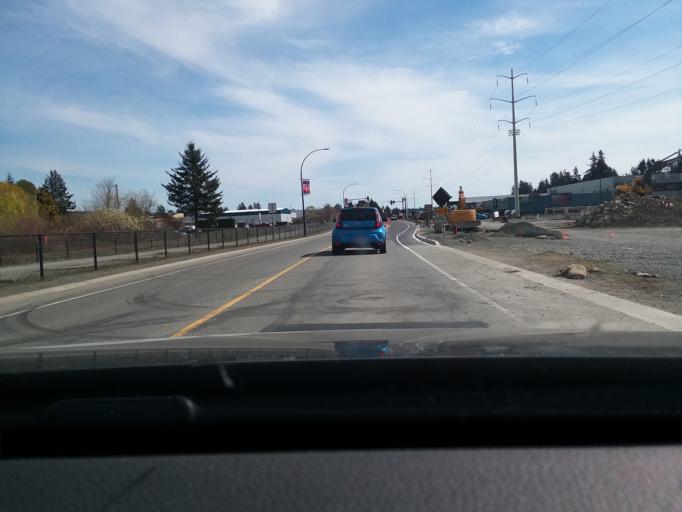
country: CA
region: British Columbia
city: Langford
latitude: 48.4438
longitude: -123.5254
